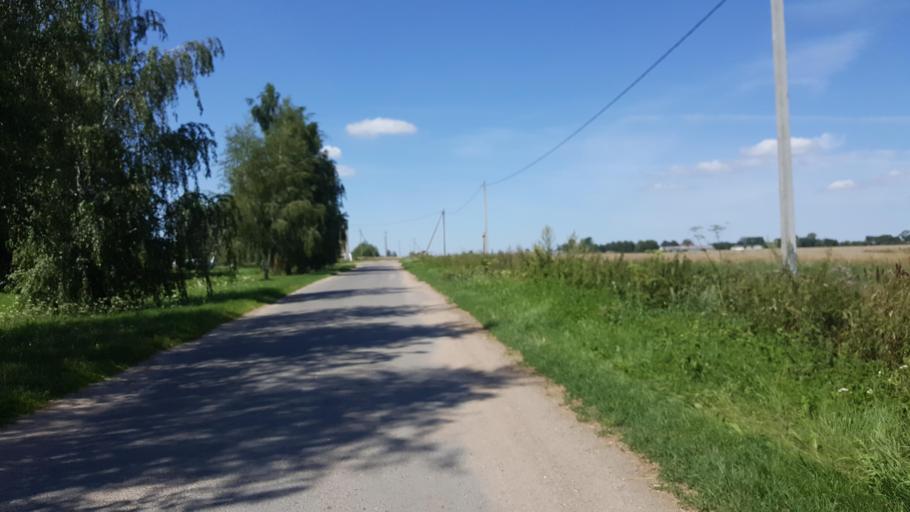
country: BY
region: Brest
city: Charnawchytsy
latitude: 52.3390
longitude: 23.6241
